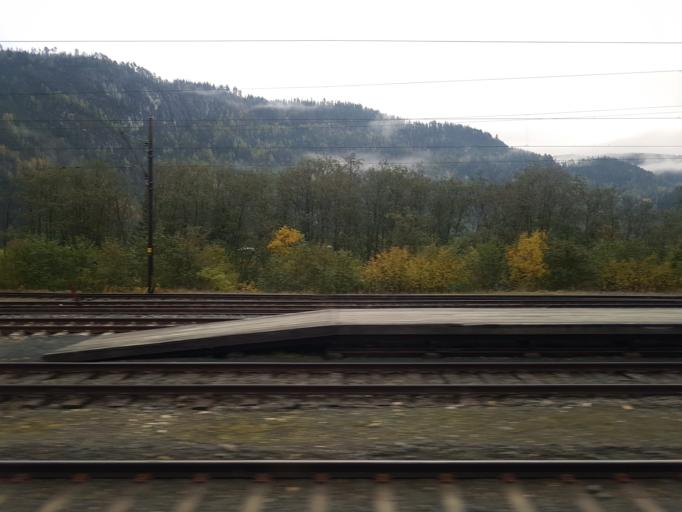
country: NO
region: Sor-Trondelag
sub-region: Midtre Gauldal
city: Storen
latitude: 63.0385
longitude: 10.2806
